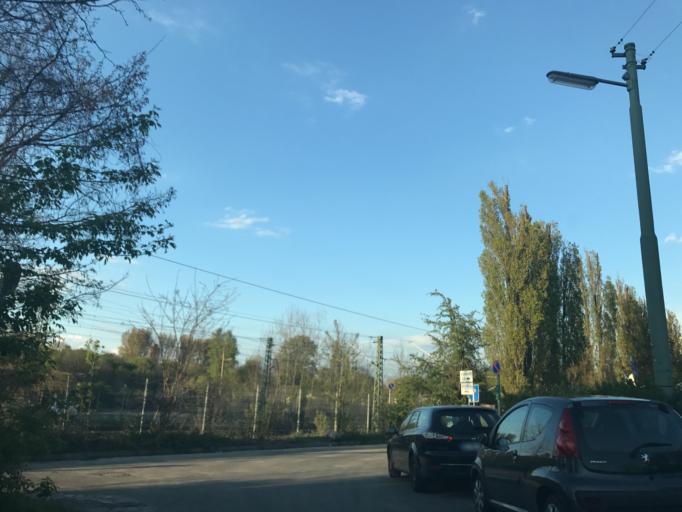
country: DE
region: Berlin
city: Siemensstadt
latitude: 52.5271
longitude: 13.2624
